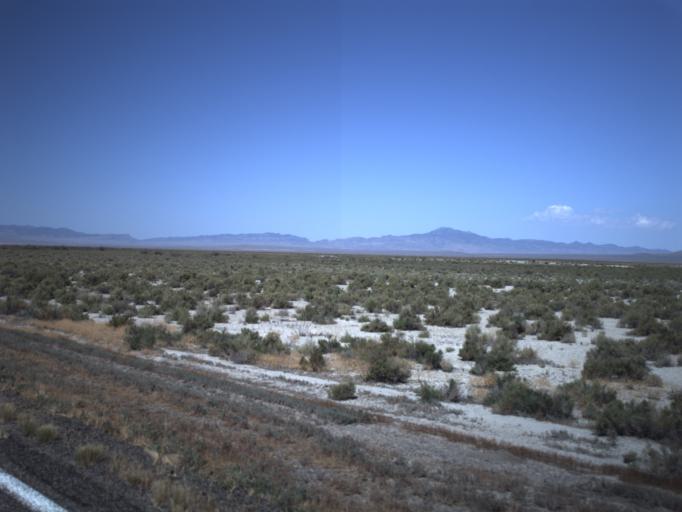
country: US
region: Utah
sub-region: Millard County
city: Delta
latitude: 39.3035
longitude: -112.8058
